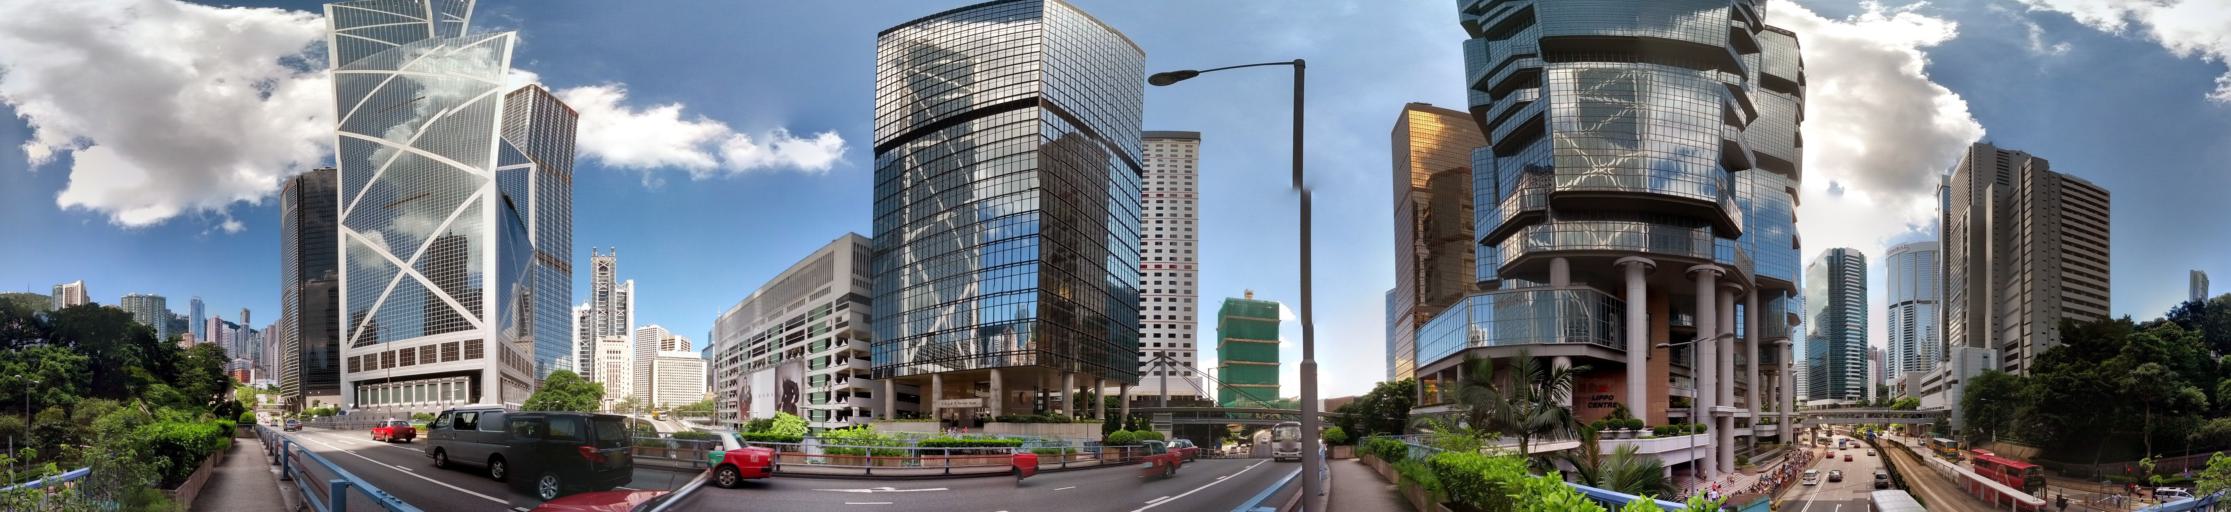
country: HK
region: Central and Western
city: Central
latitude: 22.2794
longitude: 114.1628
